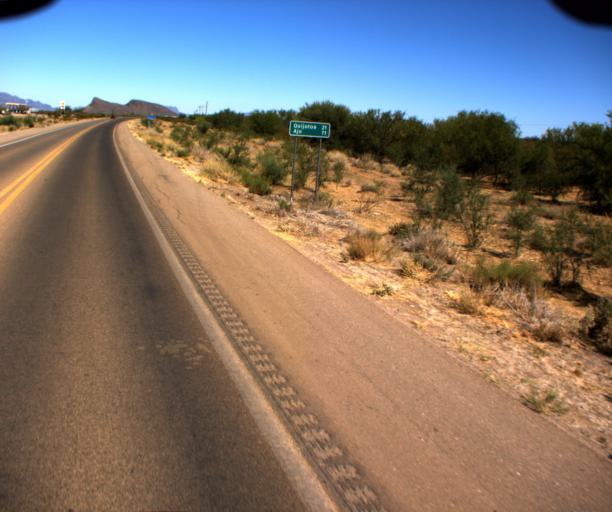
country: US
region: Arizona
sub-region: Pima County
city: Sells
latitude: 31.9233
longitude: -111.8953
